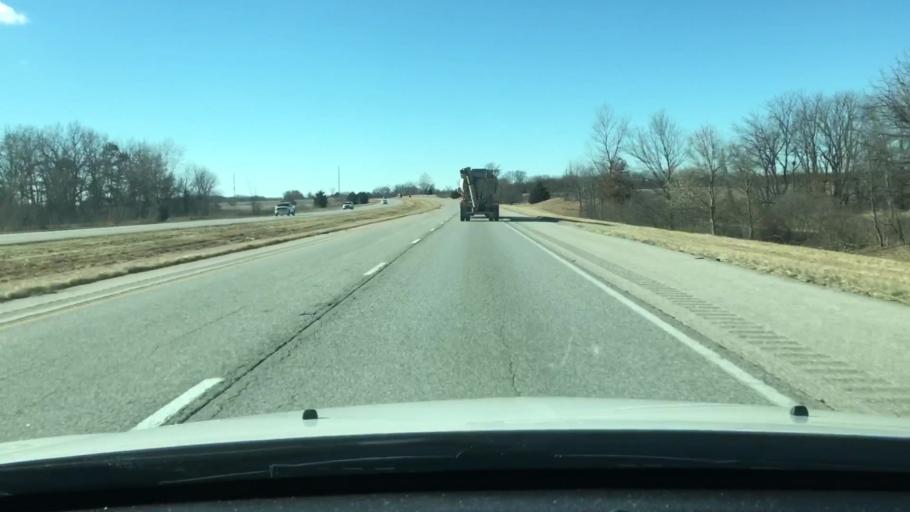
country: US
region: Illinois
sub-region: Pike County
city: Griggsville
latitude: 39.6784
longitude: -90.7180
